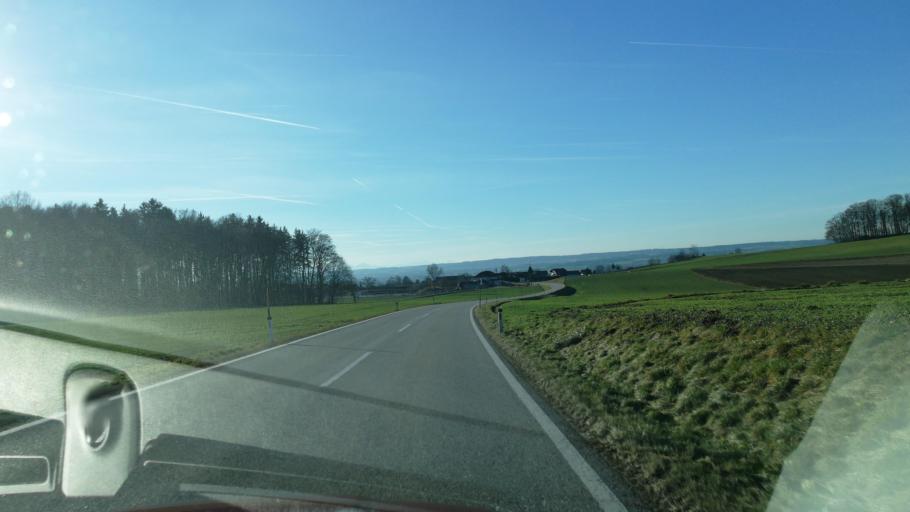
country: DE
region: Bavaria
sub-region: Upper Bavaria
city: Fridolfing
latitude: 48.0543
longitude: 12.8620
